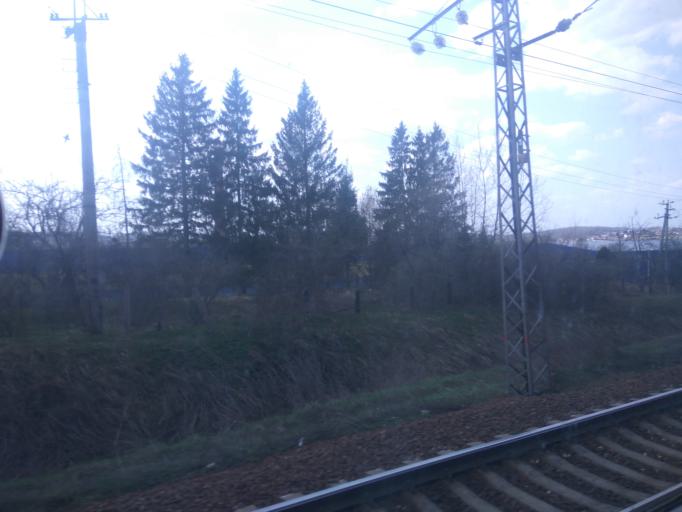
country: RU
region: Moskovskaya
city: Dedenevo
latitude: 56.2510
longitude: 37.5060
